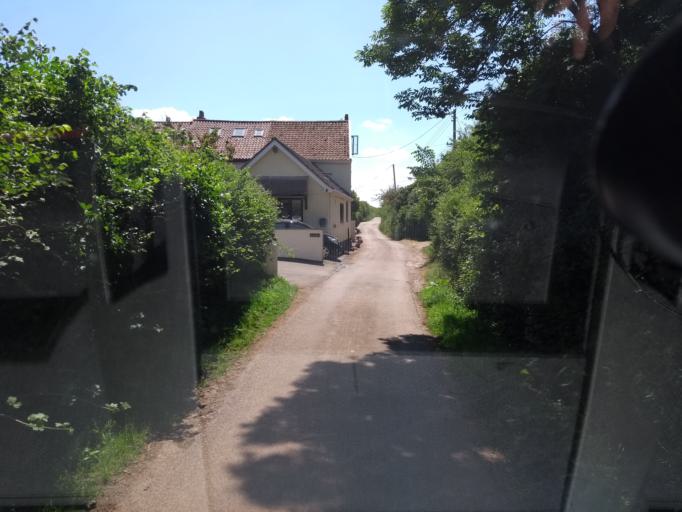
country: GB
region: England
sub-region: Somerset
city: North Petherton
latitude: 51.0639
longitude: -3.0026
